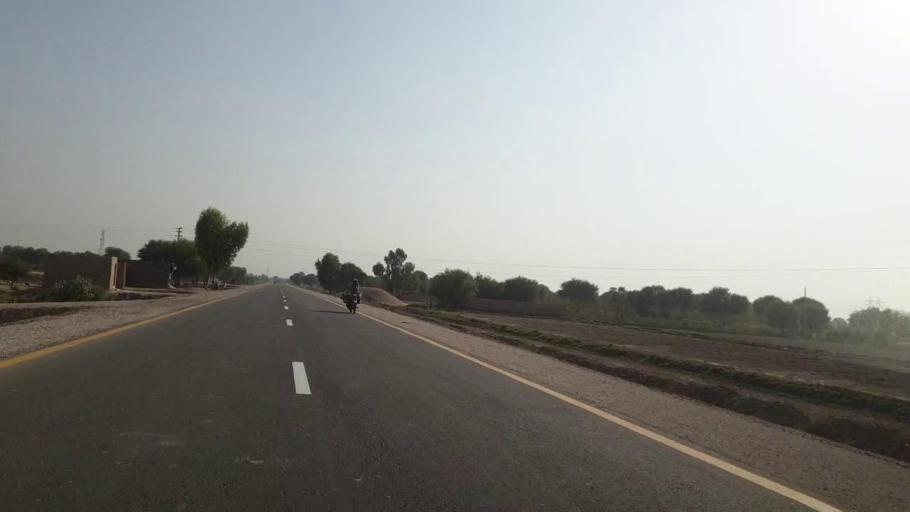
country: PK
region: Sindh
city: Bhan
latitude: 26.4889
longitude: 67.7797
